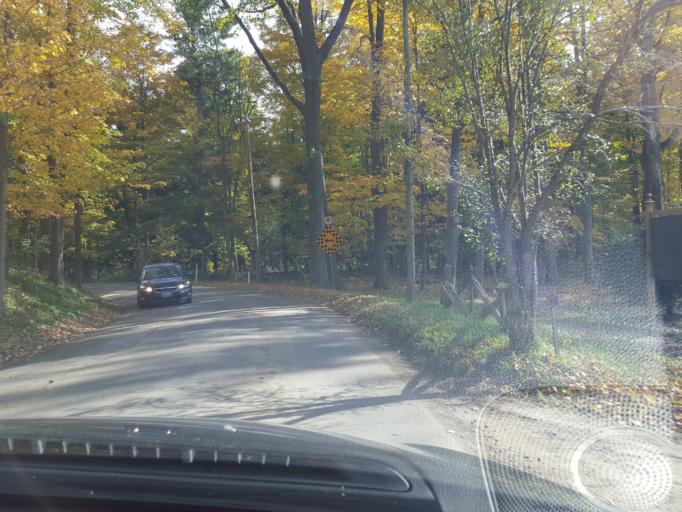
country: CA
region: Ontario
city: Ancaster
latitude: 43.2433
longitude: -80.0019
